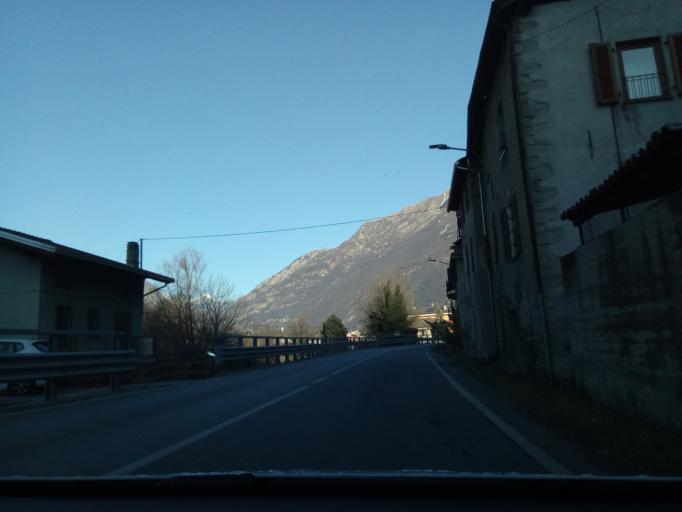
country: IT
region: Piedmont
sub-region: Provincia di Torino
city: Carema
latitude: 45.5800
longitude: 7.8090
